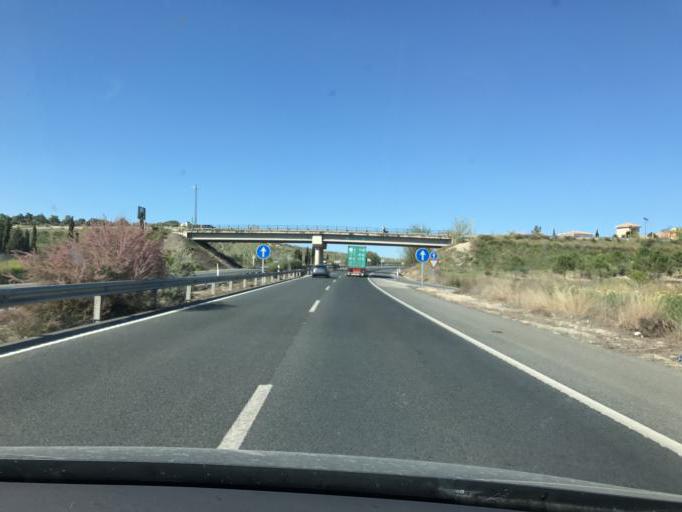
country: ES
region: Andalusia
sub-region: Provincia de Granada
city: Moraleda de Zafayona
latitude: 37.1796
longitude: -3.9001
